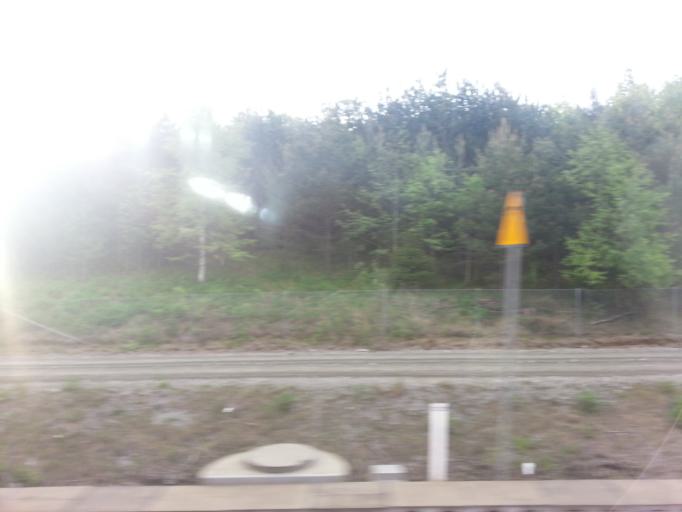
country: NO
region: Akershus
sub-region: Nannestad
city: Teigebyen
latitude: 60.1875
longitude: 11.0935
